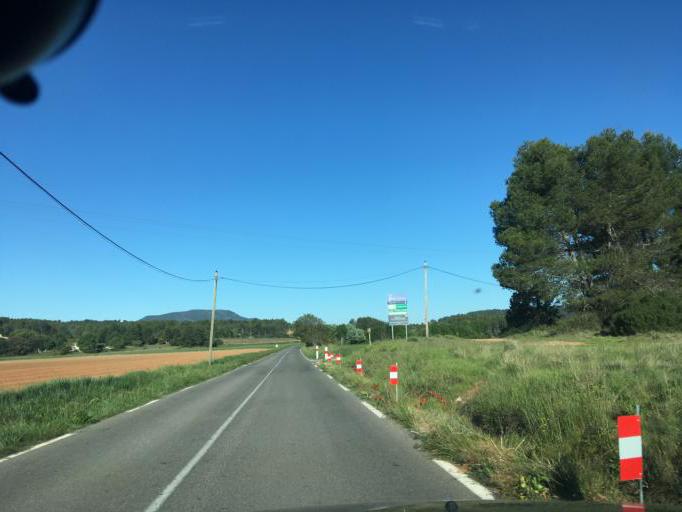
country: FR
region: Provence-Alpes-Cote d'Azur
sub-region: Departement du Var
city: Rians
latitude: 43.6115
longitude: 5.7161
